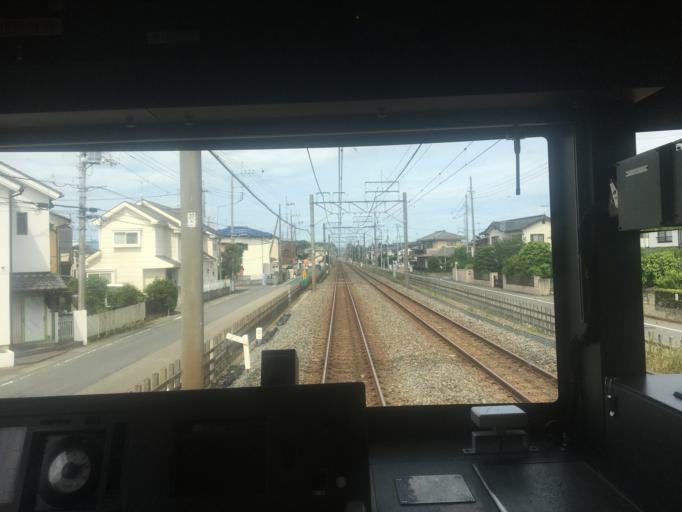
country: JP
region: Saitama
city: Fukiage-fujimi
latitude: 36.0421
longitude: 139.3910
